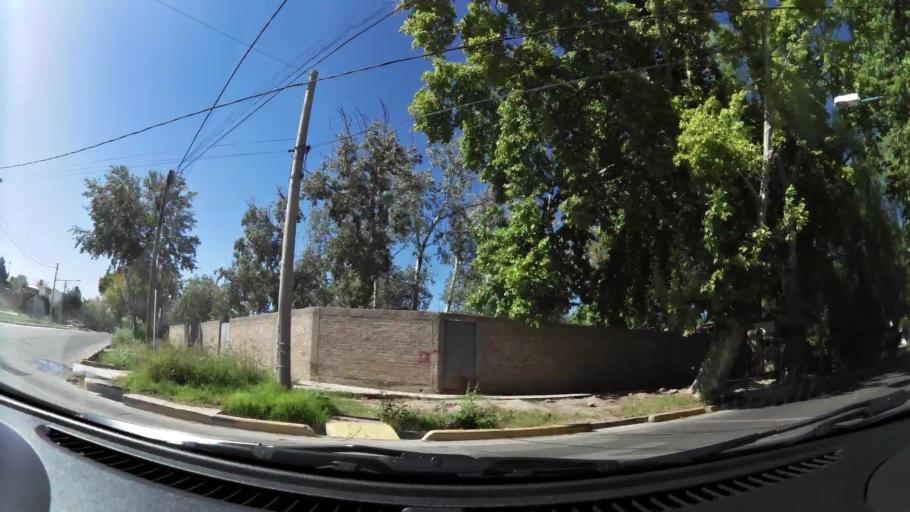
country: AR
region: Mendoza
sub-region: Departamento de Godoy Cruz
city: Godoy Cruz
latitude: -32.9570
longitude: -68.8481
